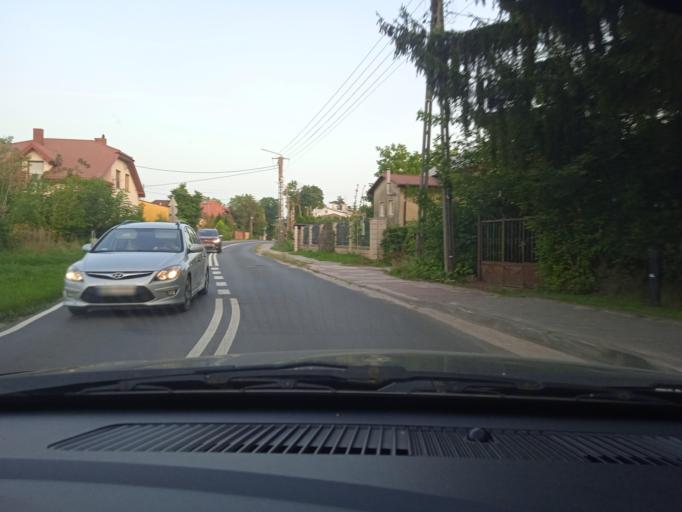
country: PL
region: Masovian Voivodeship
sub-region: Powiat nowodworski
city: Pomiechowek
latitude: 52.4746
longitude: 20.7259
